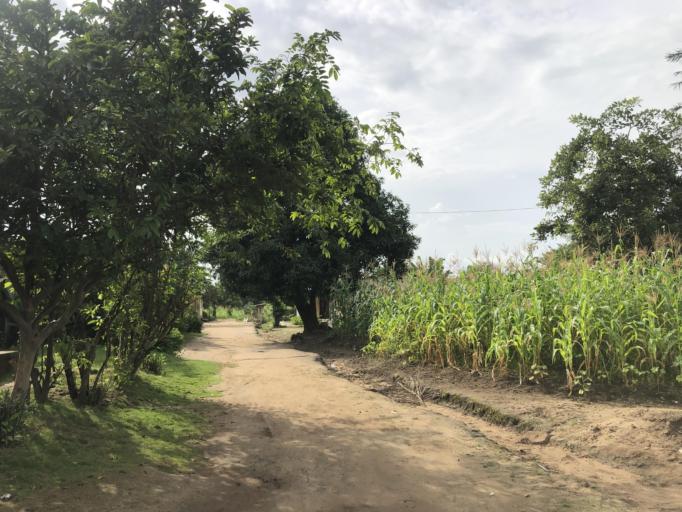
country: SL
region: Northern Province
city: Bumbuna
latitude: 9.0460
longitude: -11.7504
